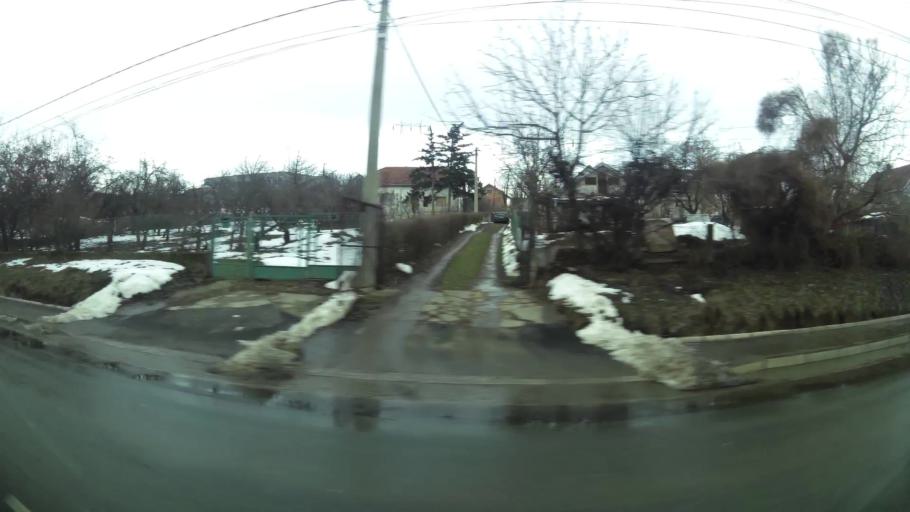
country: RS
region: Central Serbia
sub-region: Belgrade
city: Zvezdara
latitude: 44.7213
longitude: 20.5033
